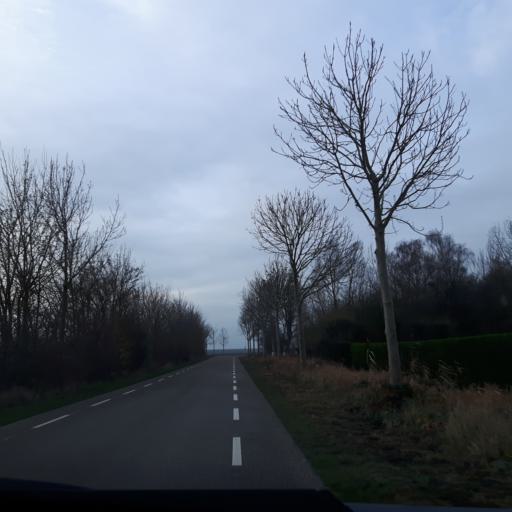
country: NL
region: Zeeland
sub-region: Gemeente Terneuzen
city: Terneuzen
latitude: 51.4016
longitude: 3.8380
